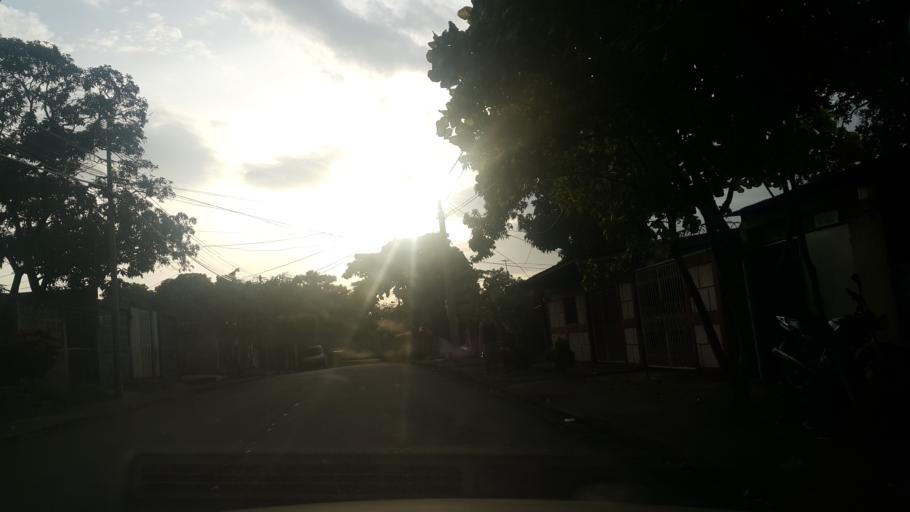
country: NI
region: Managua
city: Managua
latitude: 12.1315
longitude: -86.2977
